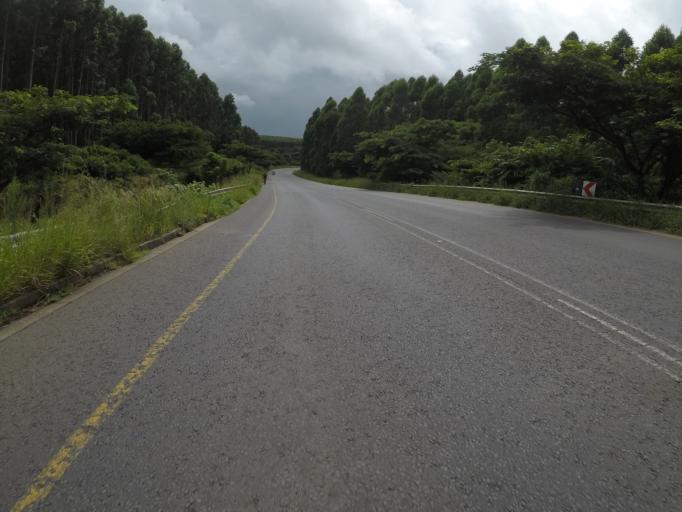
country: ZA
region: KwaZulu-Natal
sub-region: uThungulu District Municipality
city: eSikhawini
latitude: -28.8653
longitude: 31.8898
